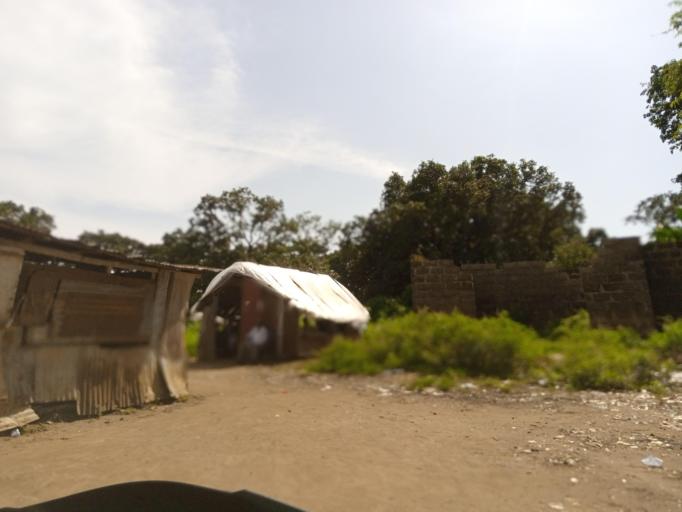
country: SL
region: Northern Province
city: Masoyila
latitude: 8.6130
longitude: -13.2024
